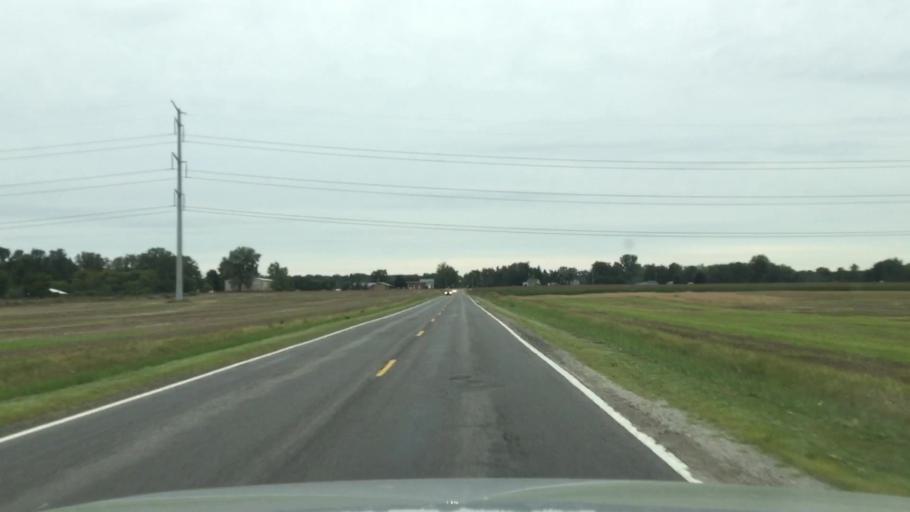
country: US
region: Michigan
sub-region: Washtenaw County
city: Milan
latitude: 42.1184
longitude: -83.6961
